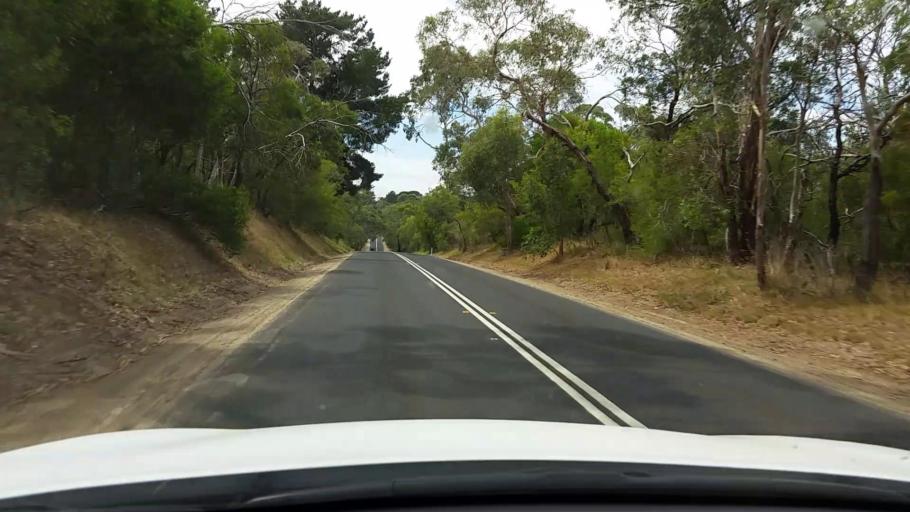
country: AU
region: Victoria
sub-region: Mornington Peninsula
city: Mount Martha
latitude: -38.2902
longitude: 145.0560
